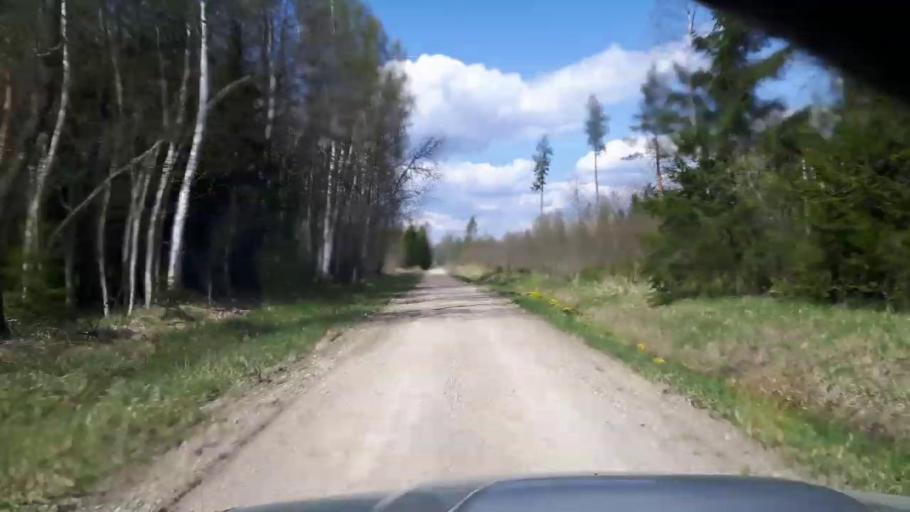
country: EE
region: Paernumaa
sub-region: Tootsi vald
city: Tootsi
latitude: 58.4495
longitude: 24.9001
